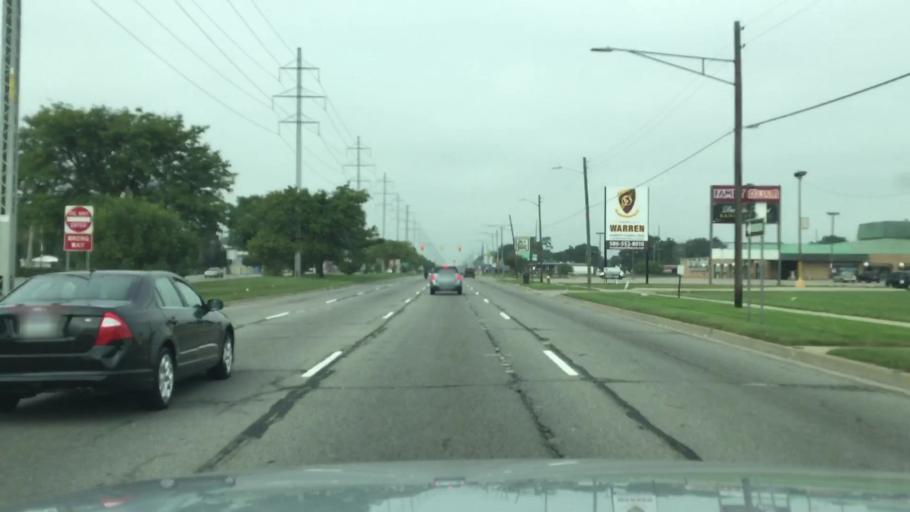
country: US
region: Michigan
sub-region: Macomb County
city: Eastpointe
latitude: 42.4497
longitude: -82.9811
